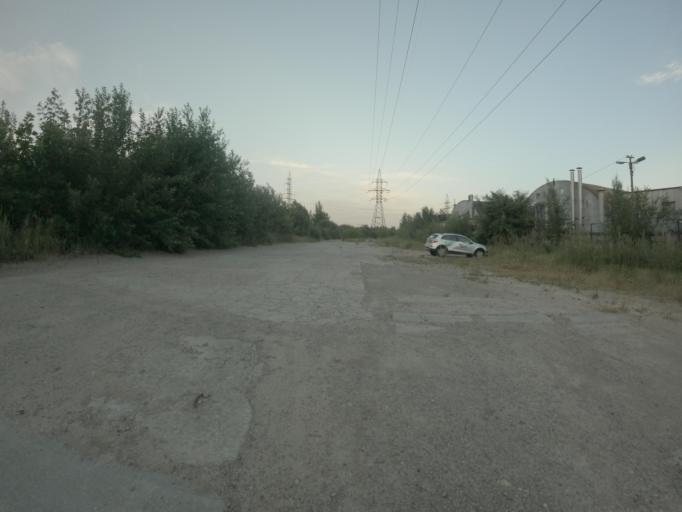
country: RU
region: St.-Petersburg
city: Krasnogvargeisky
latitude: 59.9401
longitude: 30.4426
